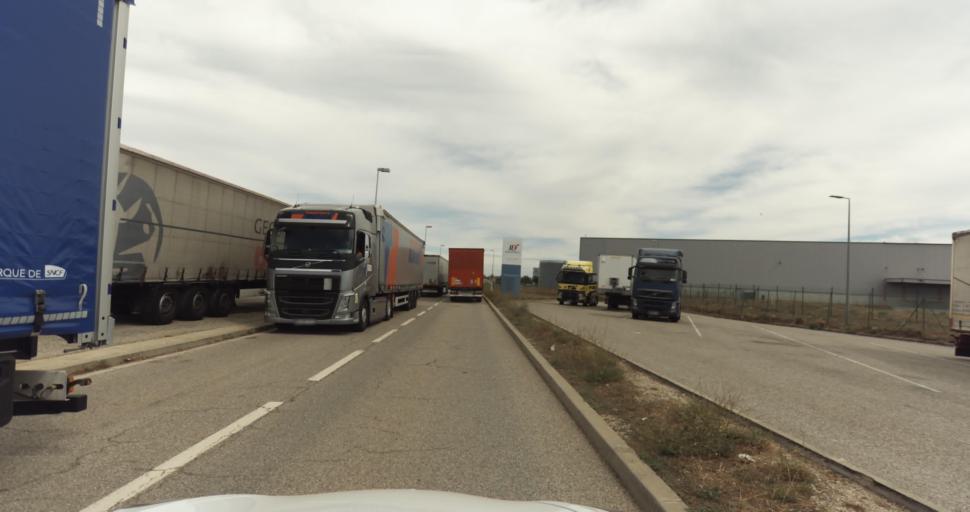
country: FR
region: Provence-Alpes-Cote d'Azur
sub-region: Departement des Bouches-du-Rhone
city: Miramas
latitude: 43.6086
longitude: 4.9932
